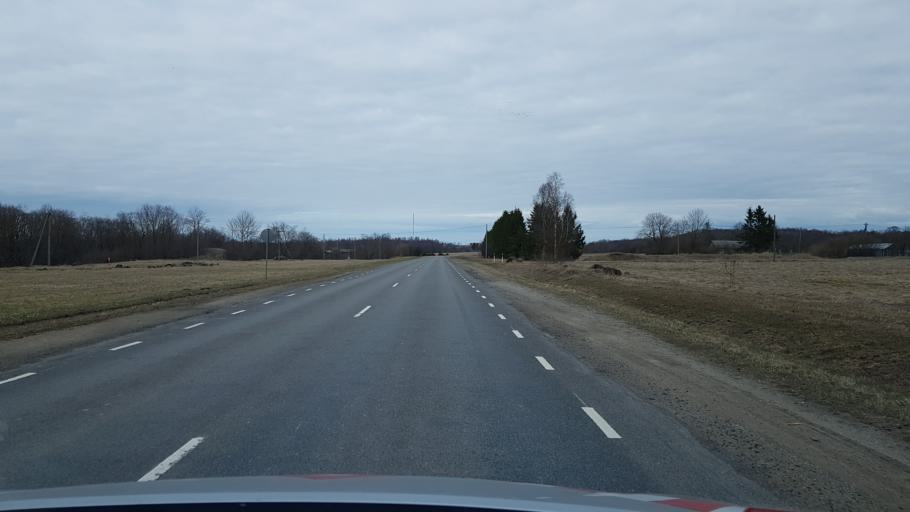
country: EE
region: Ida-Virumaa
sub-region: Sillamaee linn
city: Sillamae
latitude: 59.3786
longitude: 27.7634
